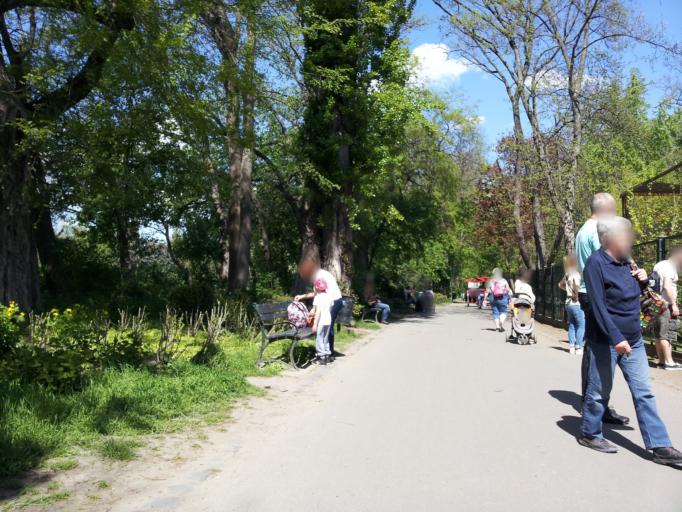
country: HU
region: Budapest
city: Budapest III. keruelet
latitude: 47.5258
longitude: 19.0496
